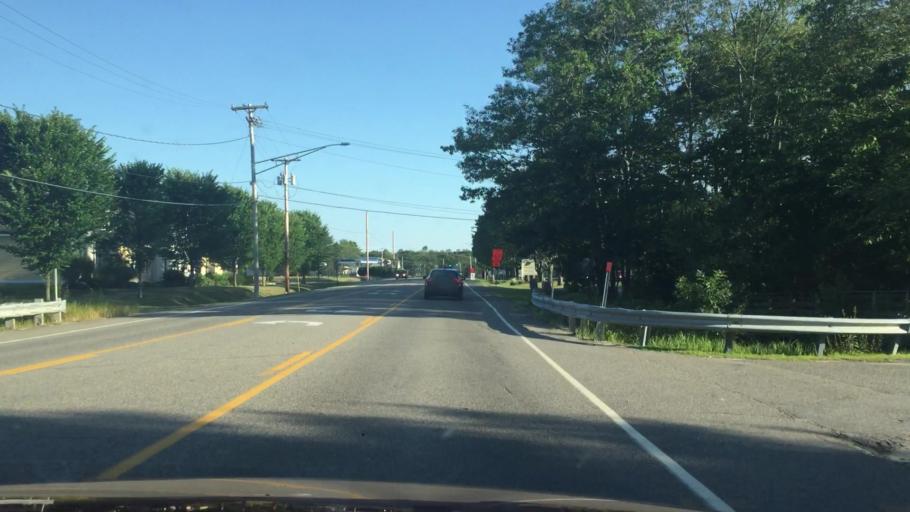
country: US
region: Maine
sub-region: Cumberland County
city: Yarmouth
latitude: 43.7959
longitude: -70.1885
